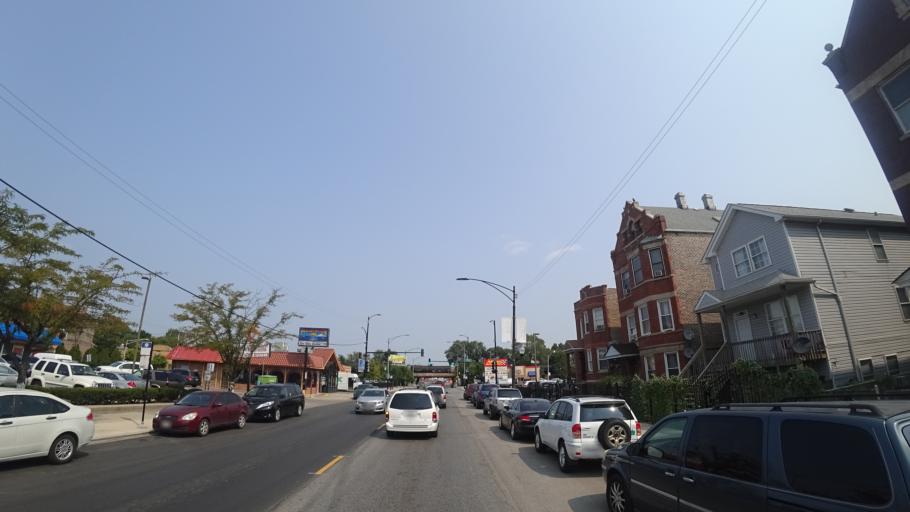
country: US
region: Illinois
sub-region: Cook County
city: Cicero
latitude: 41.8473
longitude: -87.7246
